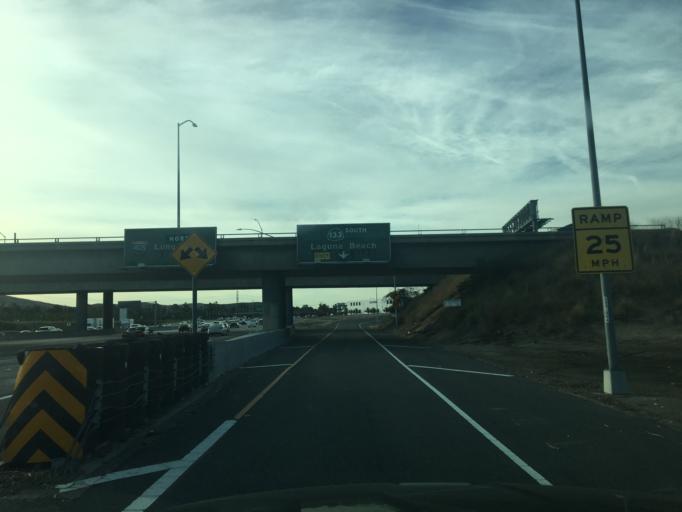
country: US
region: California
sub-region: Orange County
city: Laguna Woods
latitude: 33.6519
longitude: -117.7602
